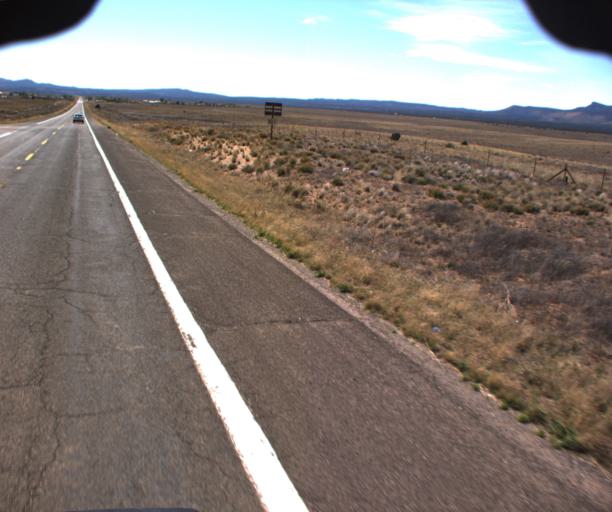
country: US
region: Arizona
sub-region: Mohave County
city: Peach Springs
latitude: 35.4923
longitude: -113.5480
